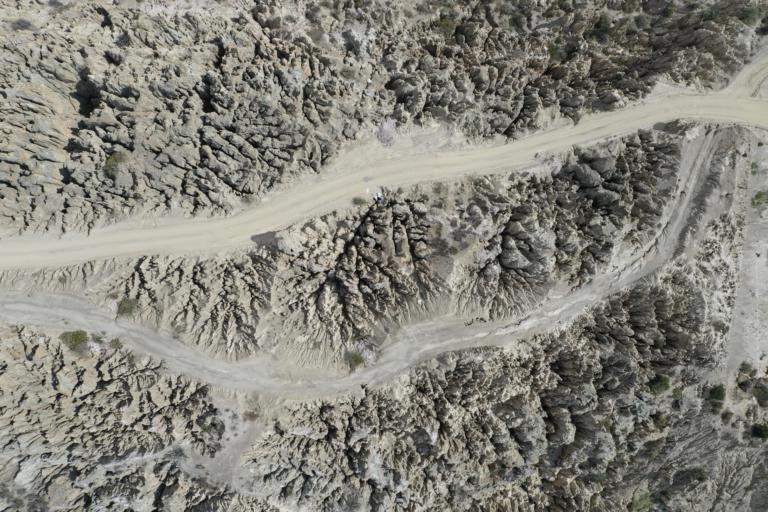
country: BO
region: La Paz
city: La Paz
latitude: -16.5649
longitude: -68.1226
